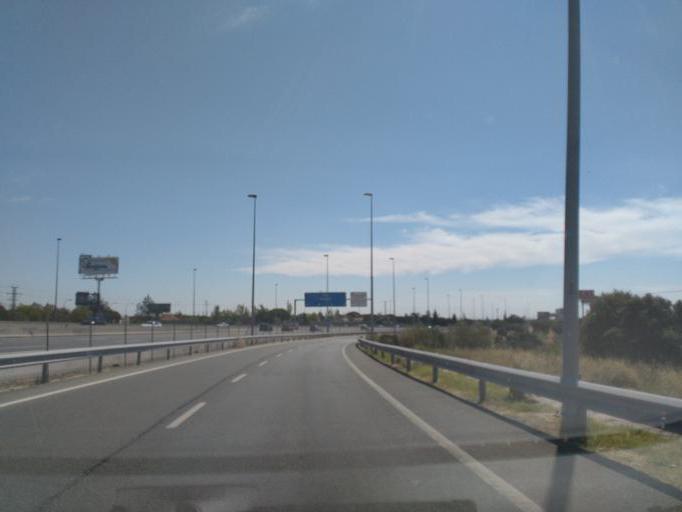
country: ES
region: Madrid
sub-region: Provincia de Madrid
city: Las Matas
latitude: 40.5623
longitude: -3.9046
